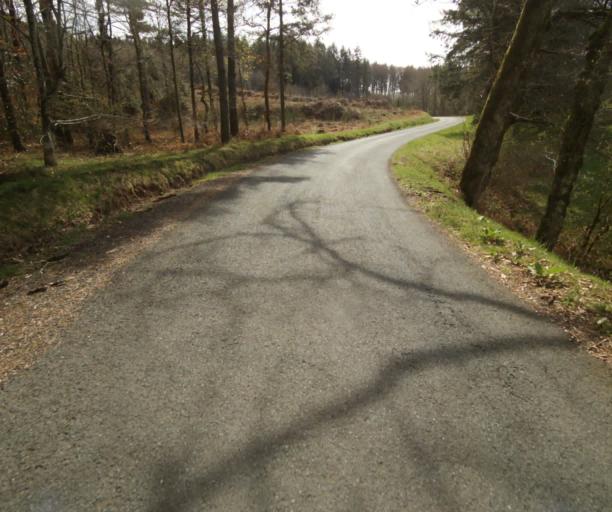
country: FR
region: Limousin
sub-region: Departement de la Correze
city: Correze
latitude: 45.3761
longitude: 1.9002
